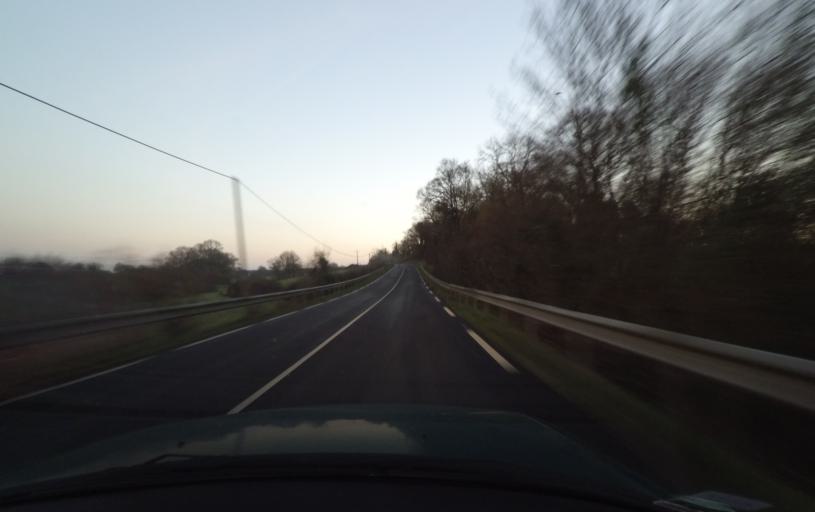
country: FR
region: Pays de la Loire
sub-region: Departement de la Mayenne
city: Soulge-sur-Ouette
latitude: 48.0937
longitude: -0.5259
